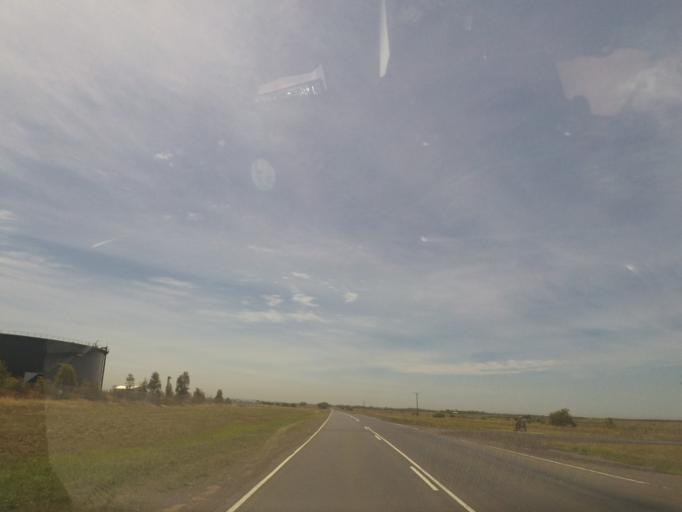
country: AU
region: Victoria
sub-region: Wyndham
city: Wyndham Vale
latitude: -37.8411
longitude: 144.5598
